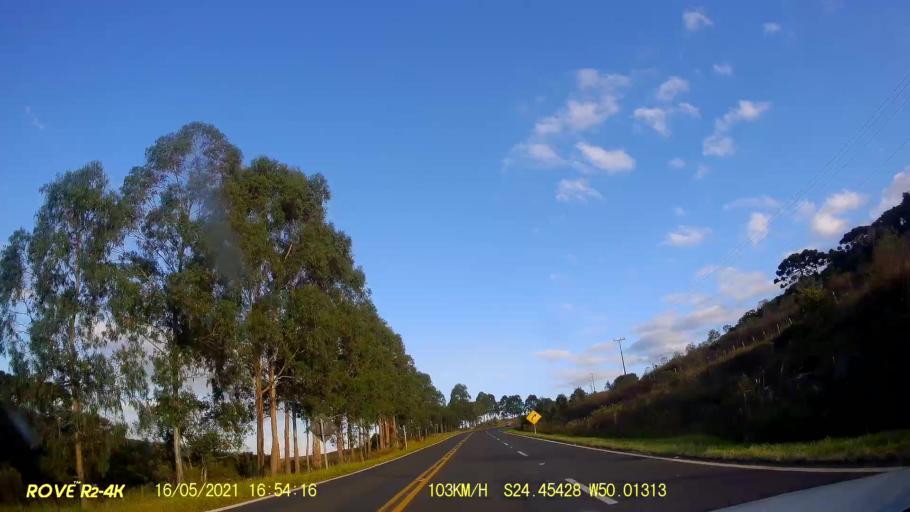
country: BR
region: Parana
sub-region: Pirai Do Sul
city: Pirai do Sul
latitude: -24.4543
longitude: -50.0133
